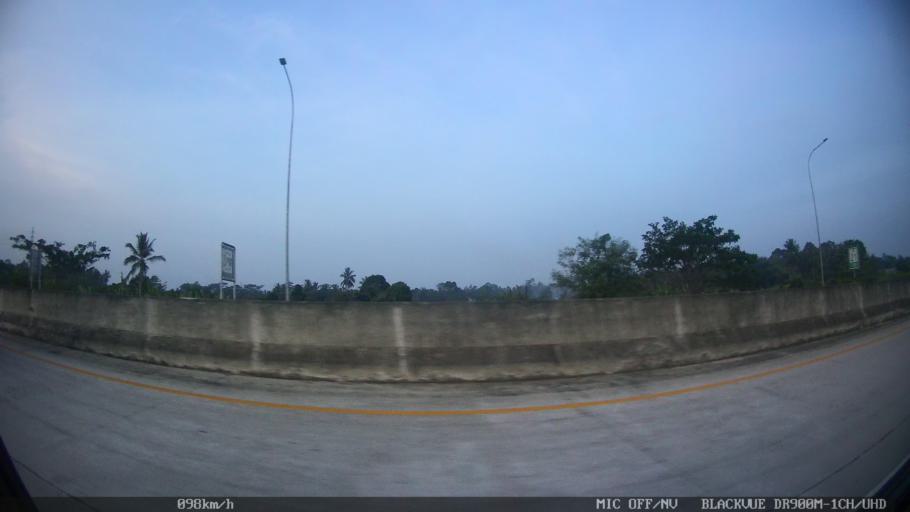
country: ID
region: Lampung
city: Pasuruan
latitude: -5.7224
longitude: 105.6649
